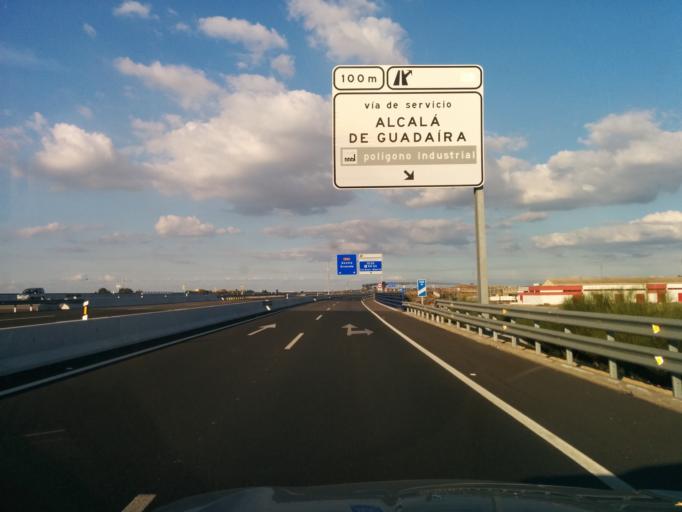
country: ES
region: Andalusia
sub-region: Provincia de Sevilla
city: Alcala de Guadaira
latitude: 37.3544
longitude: -5.8819
